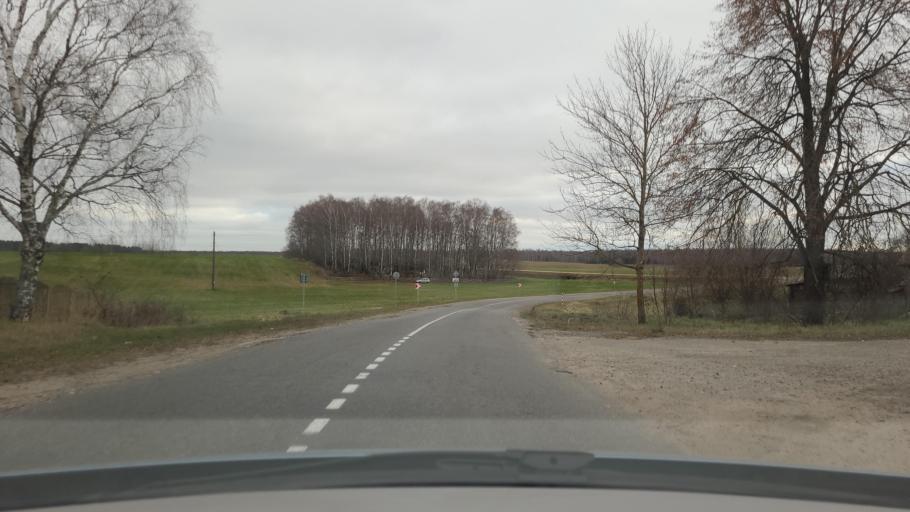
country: BY
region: Minsk
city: Khalopyenichy
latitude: 54.4692
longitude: 28.9842
